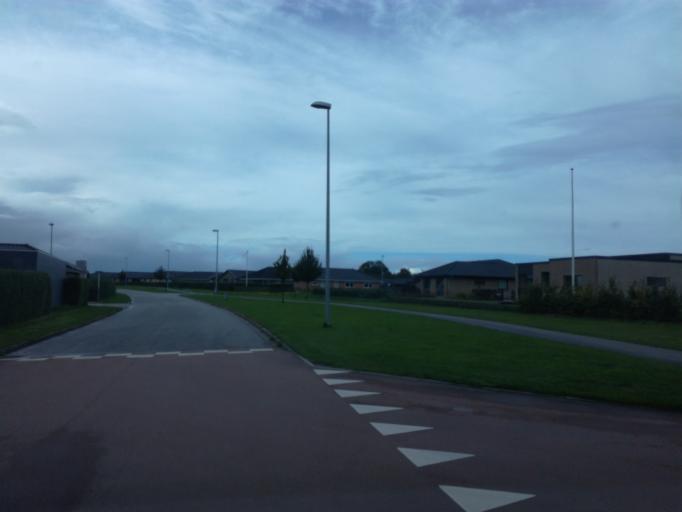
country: DK
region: South Denmark
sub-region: Fredericia Kommune
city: Fredericia
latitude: 55.5811
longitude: 9.7117
